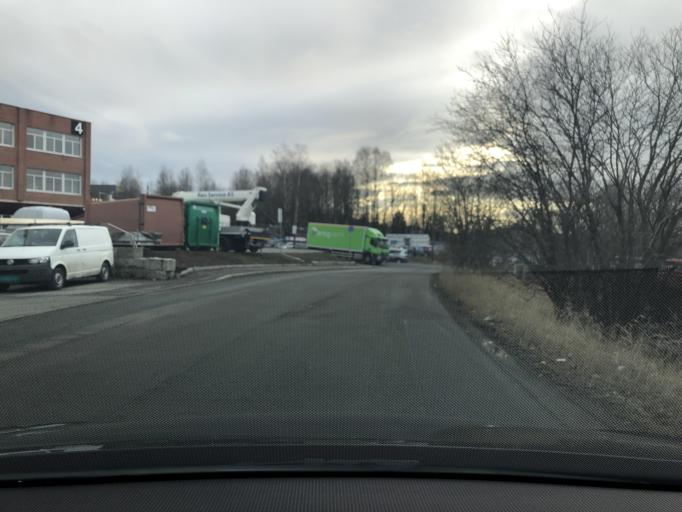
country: NO
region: Oslo
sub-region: Oslo
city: Oslo
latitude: 59.9301
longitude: 10.8458
